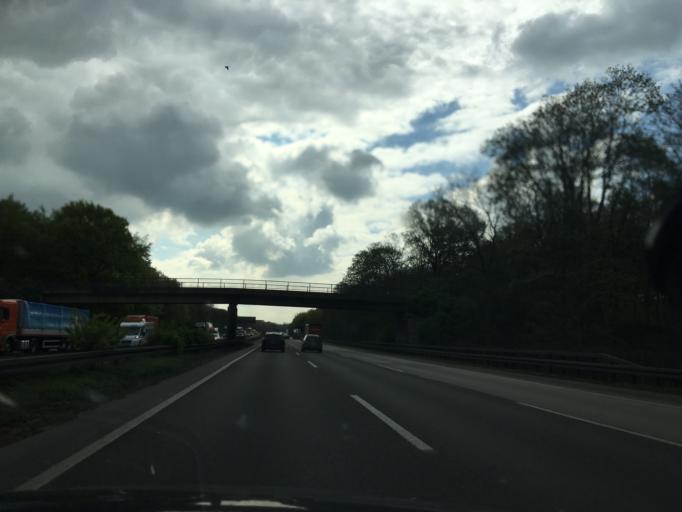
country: DE
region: North Rhine-Westphalia
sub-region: Regierungsbezirk Dusseldorf
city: Duisburg
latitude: 51.4033
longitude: 6.8066
